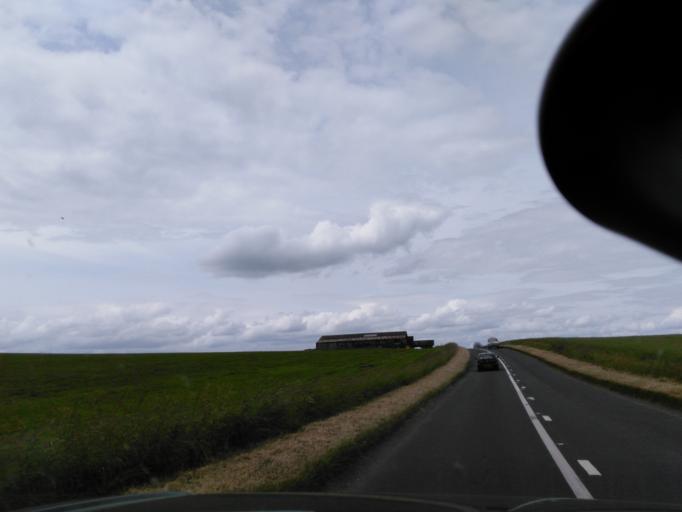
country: GB
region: England
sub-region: Wiltshire
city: Shrewton
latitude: 51.2087
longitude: -1.9359
